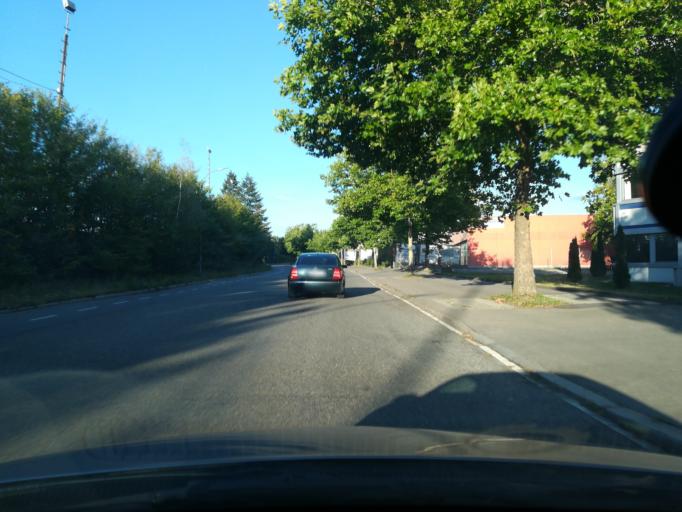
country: DE
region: Baden-Wuerttemberg
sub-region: Freiburg Region
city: Singen
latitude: 47.7577
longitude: 8.8618
